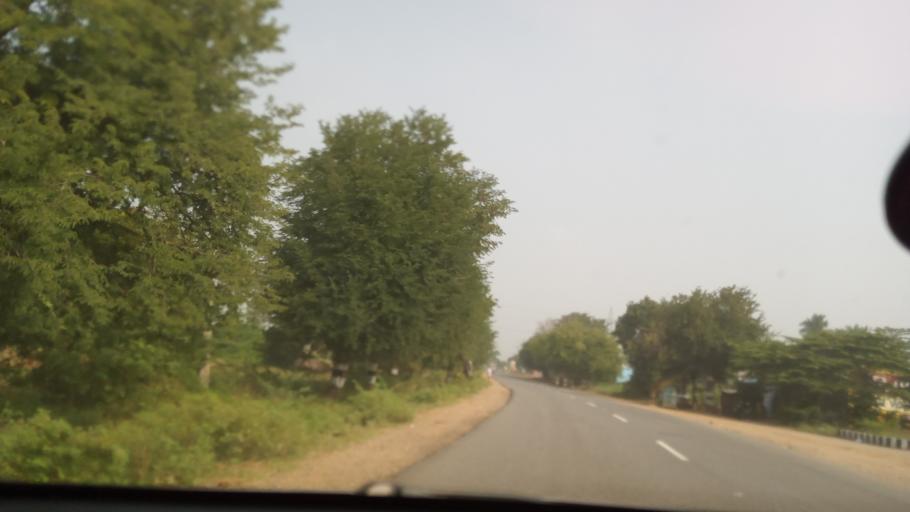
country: IN
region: Tamil Nadu
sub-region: Erode
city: Punjai Puliyampatti
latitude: 11.4062
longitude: 77.1928
